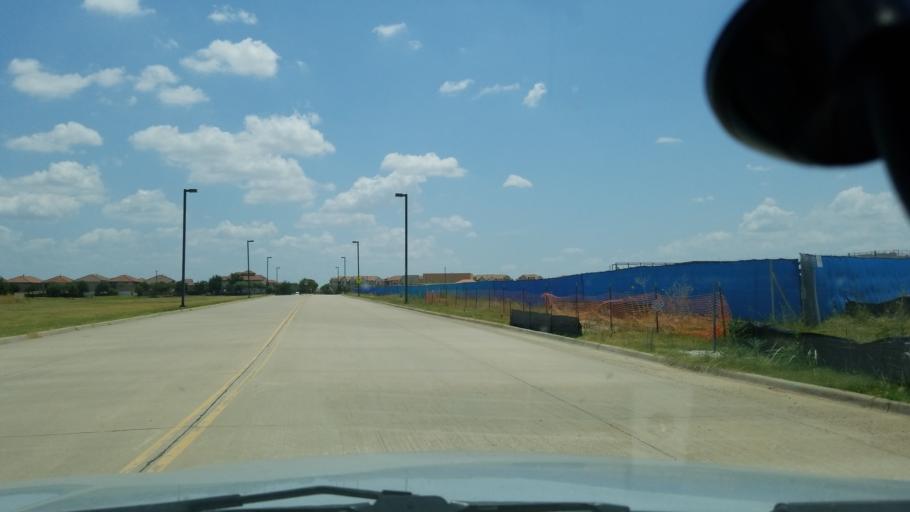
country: US
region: Texas
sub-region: Dallas County
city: Farmers Branch
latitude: 32.9060
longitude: -96.9401
